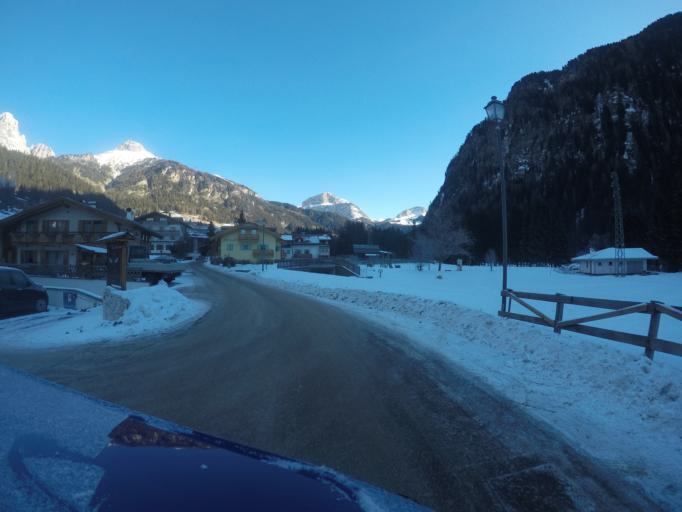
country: IT
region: Trentino-Alto Adige
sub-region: Provincia di Trento
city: Campitello di Fassa
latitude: 46.4711
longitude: 11.7341
